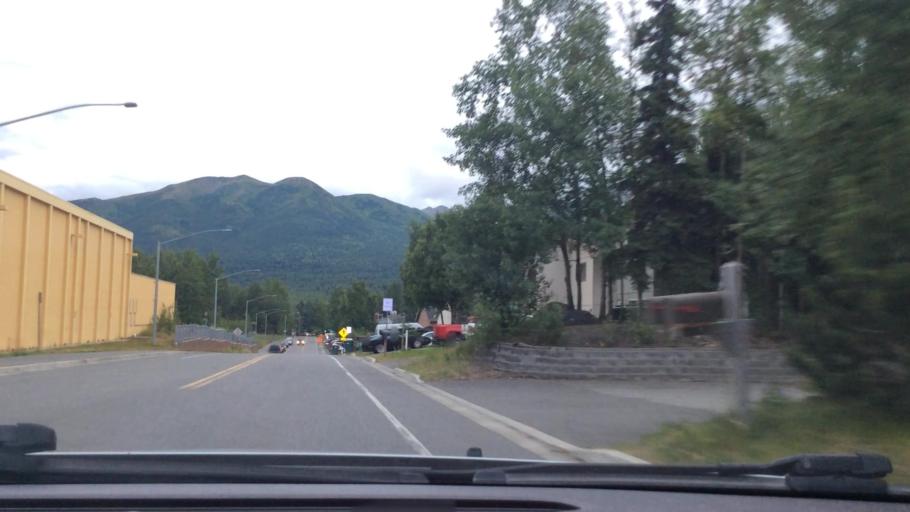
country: US
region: Alaska
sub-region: Anchorage Municipality
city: Elmendorf Air Force Base
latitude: 61.1919
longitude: -149.7319
